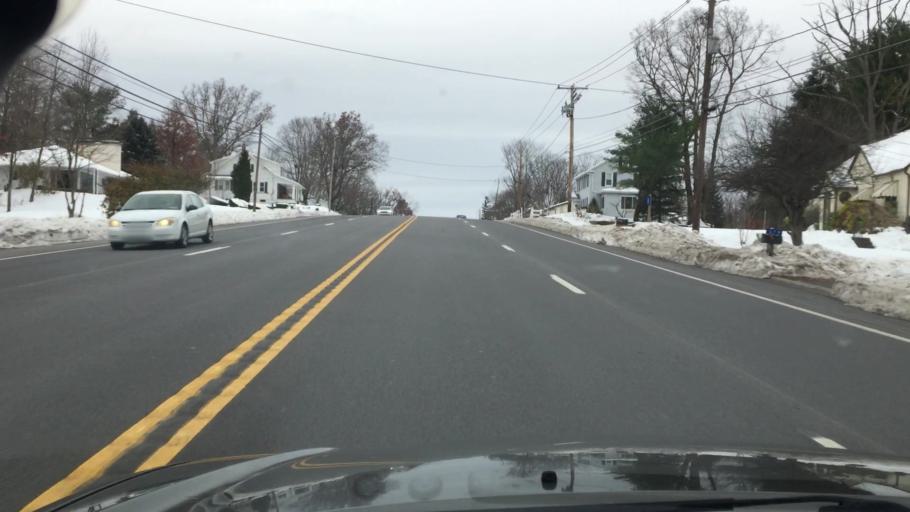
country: US
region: Pennsylvania
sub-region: Luzerne County
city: Oakdale
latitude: 41.0438
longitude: -75.9554
